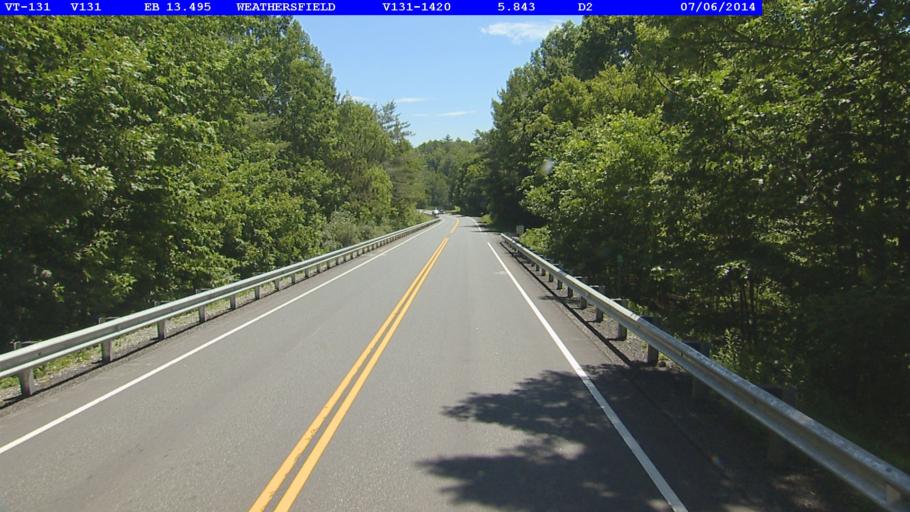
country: US
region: Vermont
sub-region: Windsor County
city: Windsor
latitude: 43.4132
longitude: -72.4562
